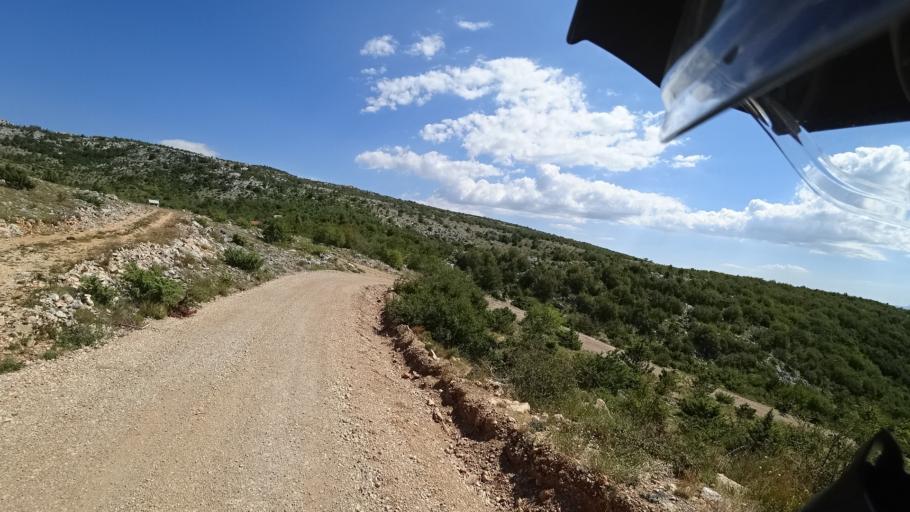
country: HR
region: Splitsko-Dalmatinska
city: Hrvace
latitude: 43.7623
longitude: 16.4686
